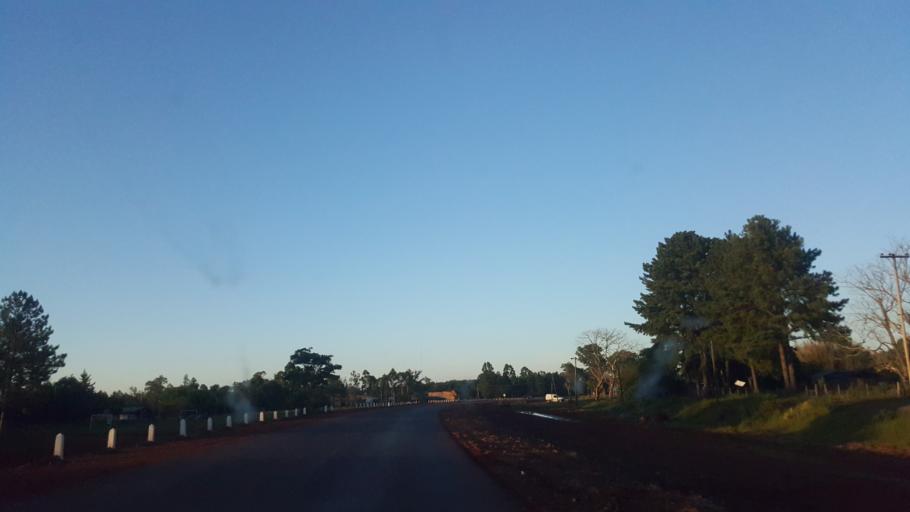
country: AR
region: Corrientes
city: Santo Tome
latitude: -28.5114
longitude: -56.0598
